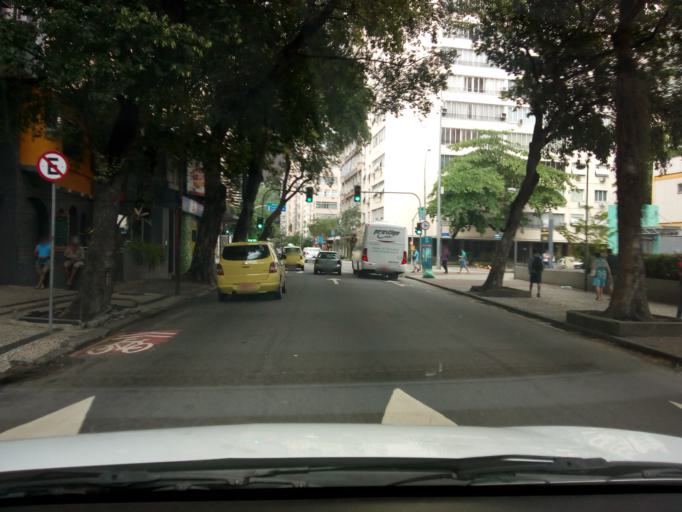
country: BR
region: Rio de Janeiro
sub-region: Rio De Janeiro
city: Rio de Janeiro
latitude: -22.9678
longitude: -43.1872
